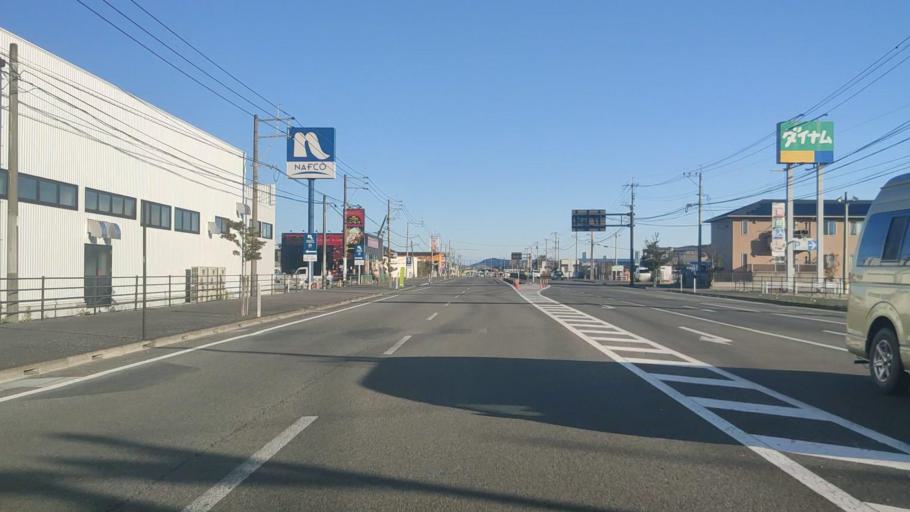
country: JP
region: Miyazaki
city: Nobeoka
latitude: 32.3972
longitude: 131.6295
